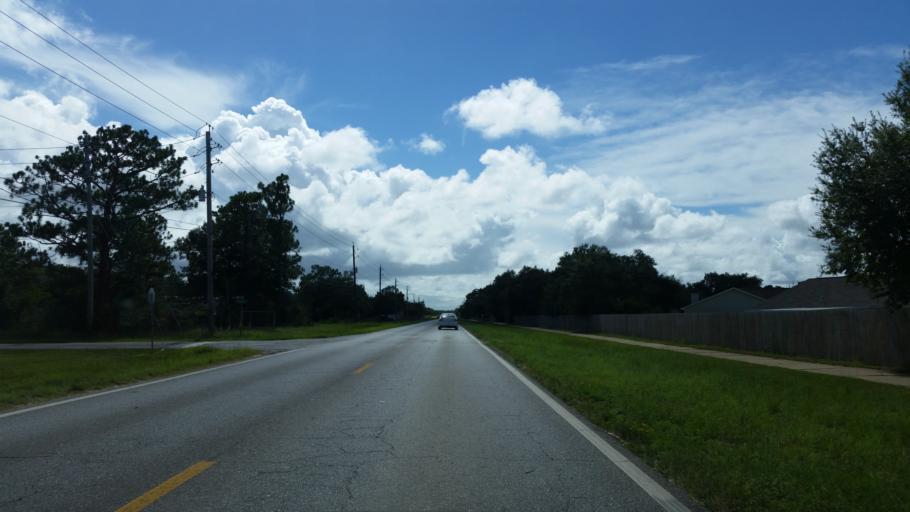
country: US
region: Florida
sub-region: Santa Rosa County
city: Holley
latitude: 30.4325
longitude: -86.8782
